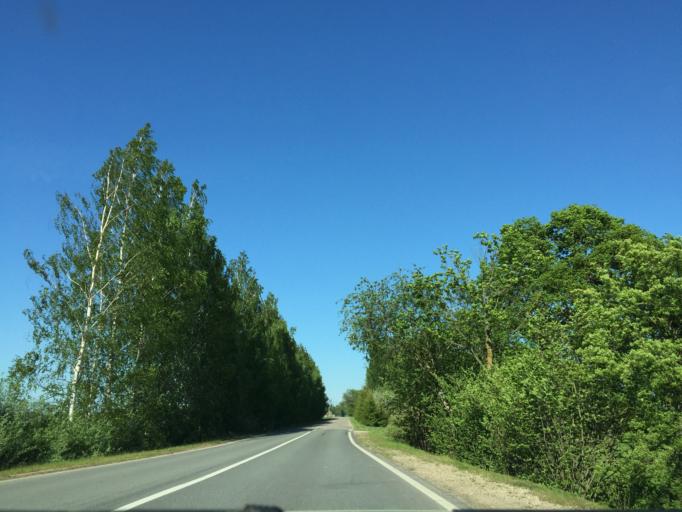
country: LV
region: Jelgava
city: Jelgava
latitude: 56.5388
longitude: 23.7078
